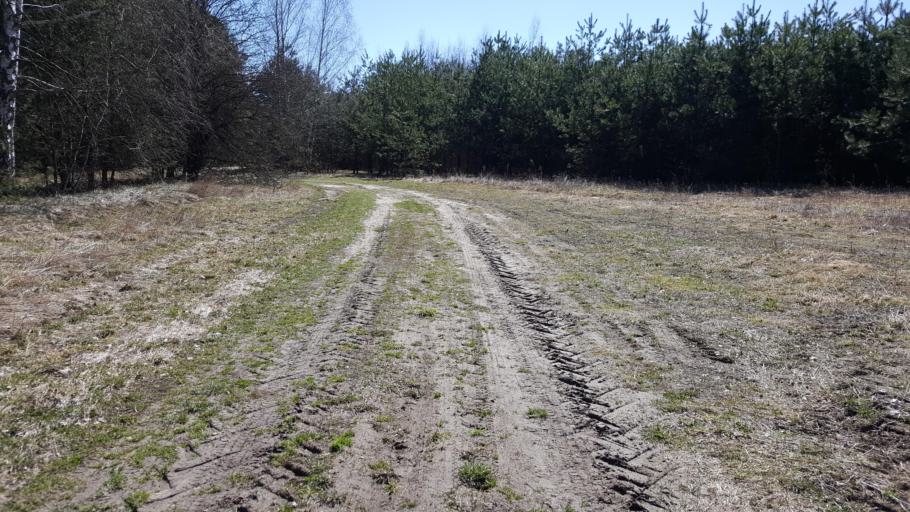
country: BY
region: Brest
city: Kamyanyets
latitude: 52.3262
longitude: 23.8558
